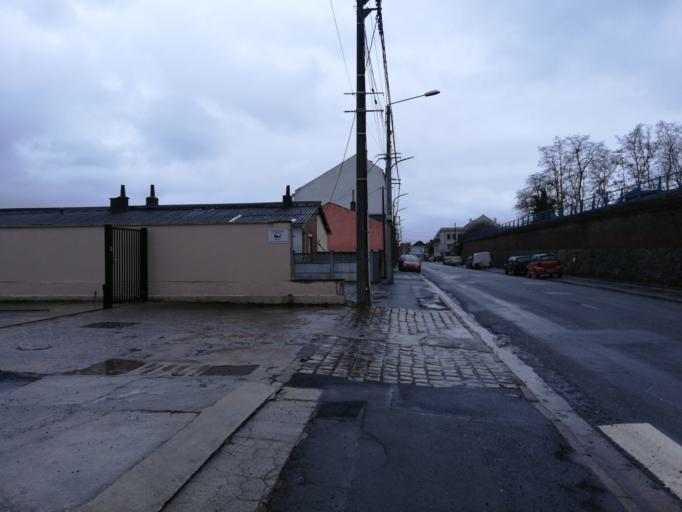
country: FR
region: Nord-Pas-de-Calais
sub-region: Departement du Pas-de-Calais
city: Montigny-en-Gohelle
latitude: 50.4275
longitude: 2.9393
